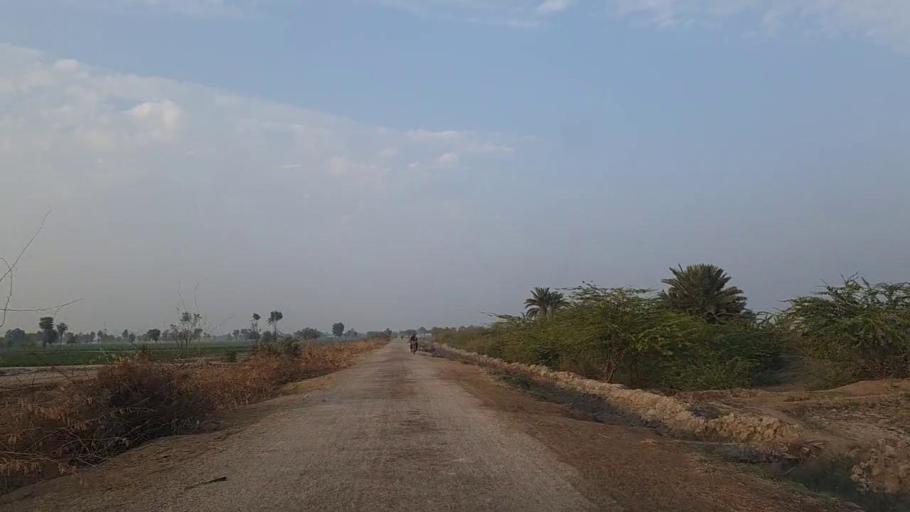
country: PK
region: Sindh
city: Jam Sahib
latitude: 26.3069
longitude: 68.6088
